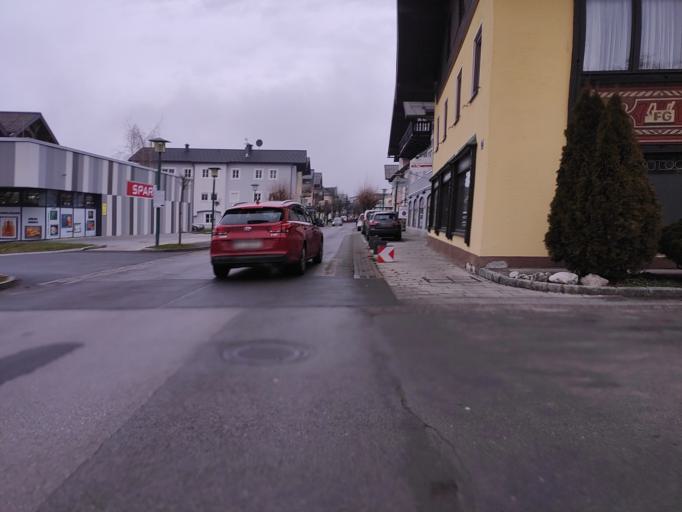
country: AT
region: Salzburg
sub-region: Politischer Bezirk Salzburg-Umgebung
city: Neumarkt am Wallersee
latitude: 47.9421
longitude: 13.2238
